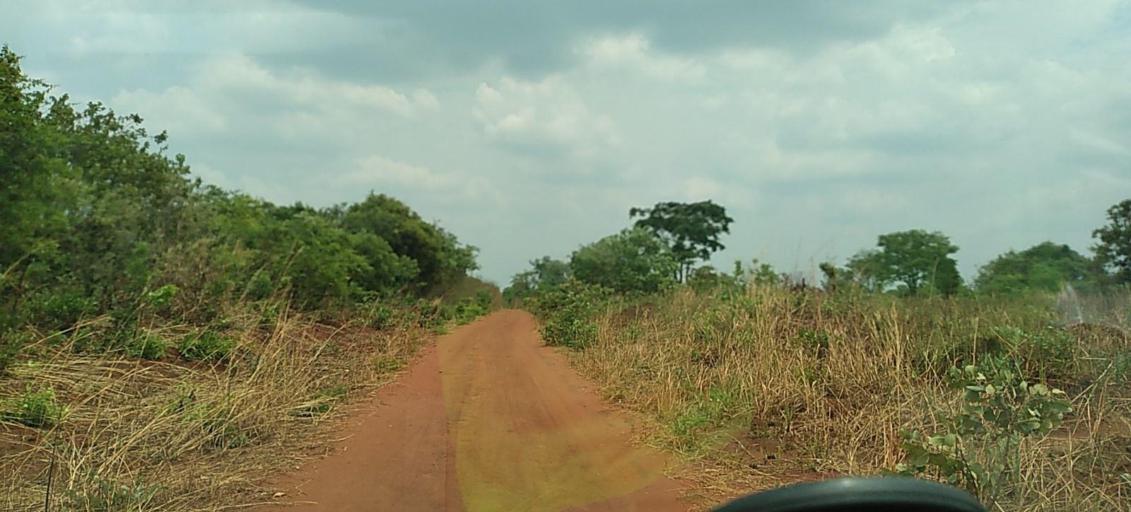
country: ZM
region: North-Western
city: Kansanshi
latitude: -12.0438
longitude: 26.3864
